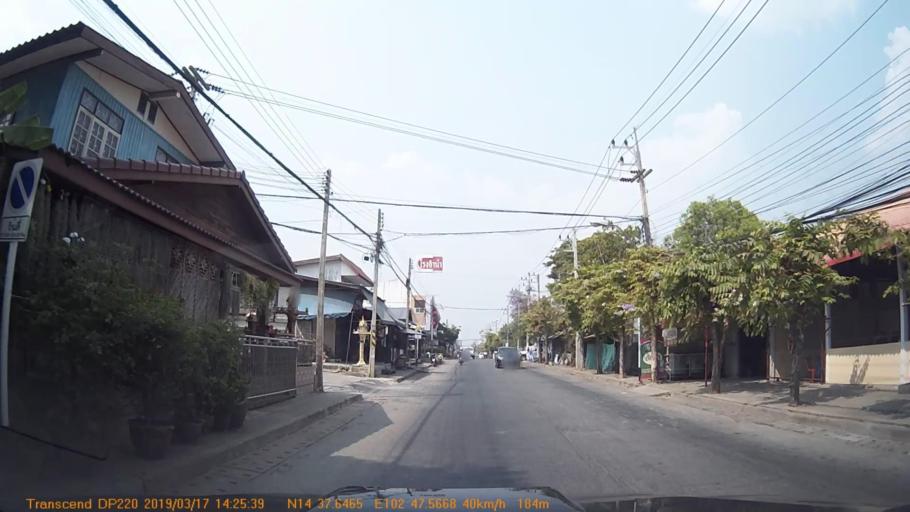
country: TH
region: Buriram
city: Nang Rong
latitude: 14.6276
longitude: 102.7928
